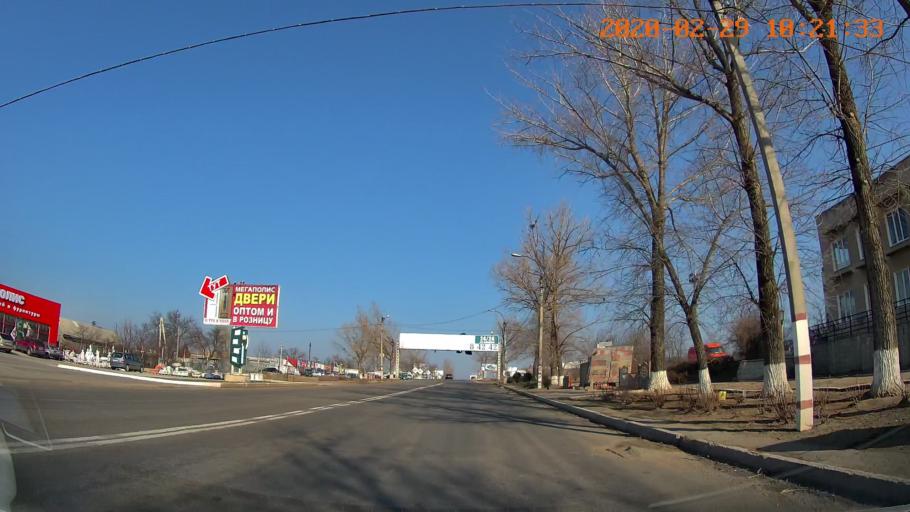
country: MD
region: Telenesti
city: Tiraspolul Nou
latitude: 46.8675
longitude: 29.6091
